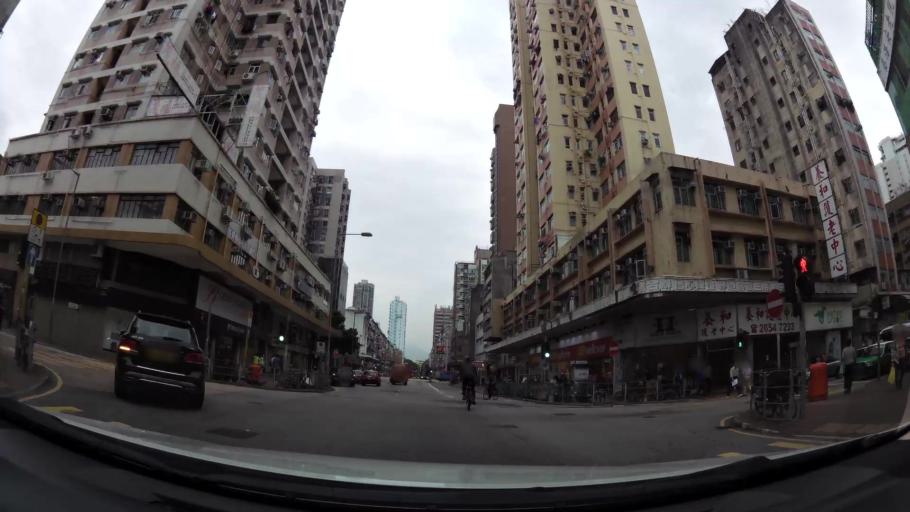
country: HK
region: Tai Po
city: Tai Po
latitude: 22.4493
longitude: 114.1656
